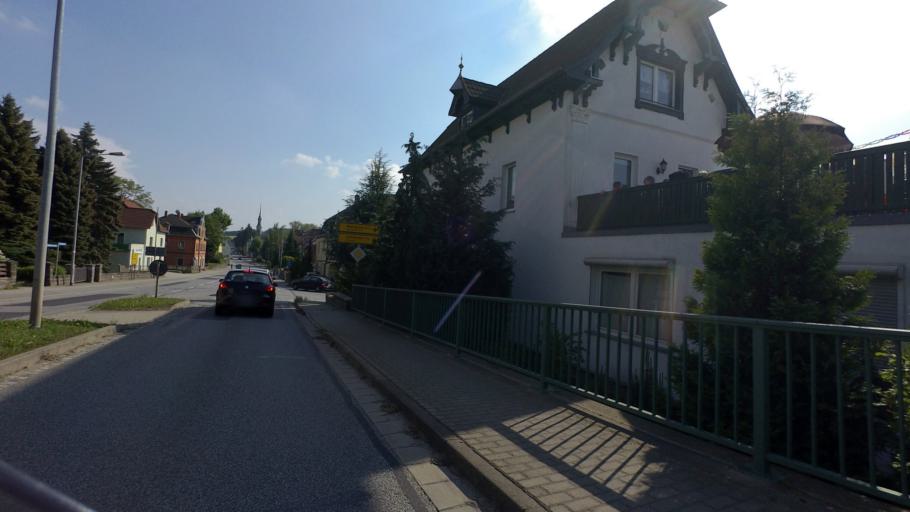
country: DE
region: Saxony
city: Grosspostwitz
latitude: 51.1238
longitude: 14.4405
